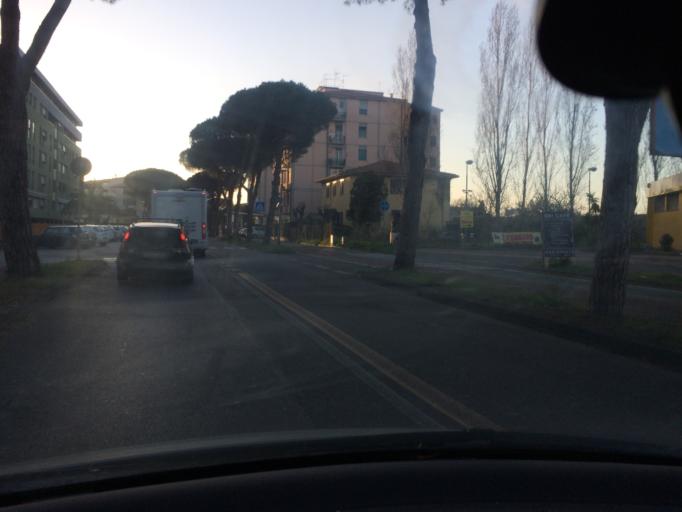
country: IT
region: Tuscany
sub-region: Province of Pisa
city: Pisa
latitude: 43.7212
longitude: 10.4198
